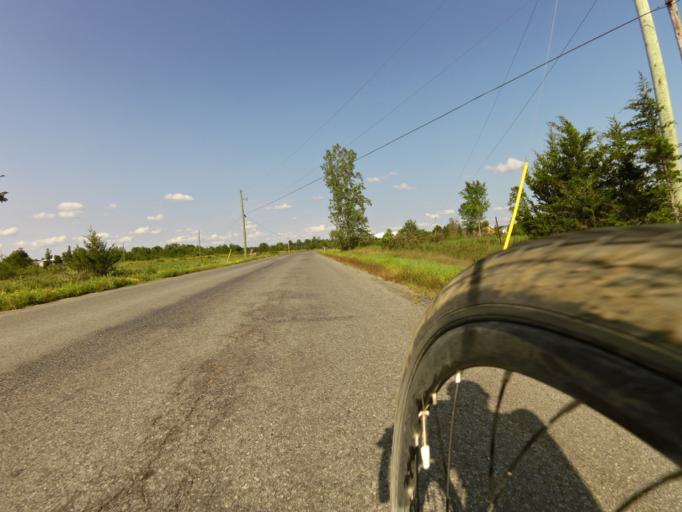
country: CA
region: Ontario
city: Kingston
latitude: 44.3418
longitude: -76.6583
